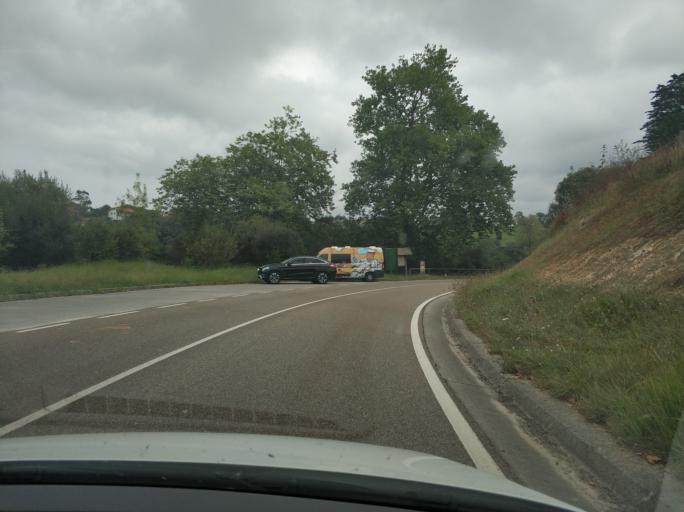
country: ES
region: Cantabria
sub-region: Provincia de Cantabria
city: Comillas
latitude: 43.3820
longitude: -4.3193
